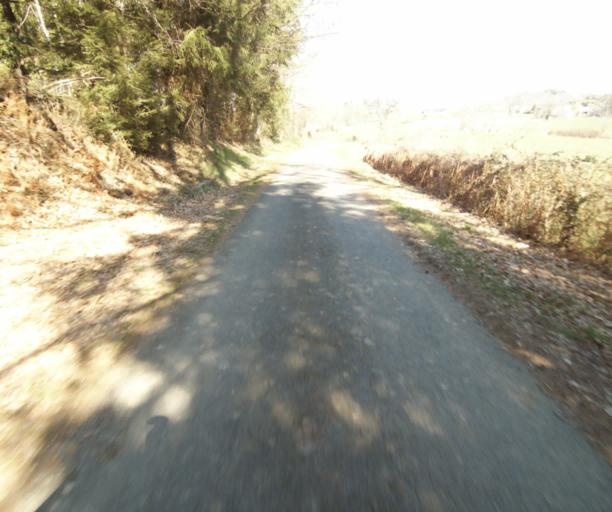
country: FR
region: Limousin
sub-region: Departement de la Correze
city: Saint-Mexant
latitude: 45.3025
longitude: 1.5995
